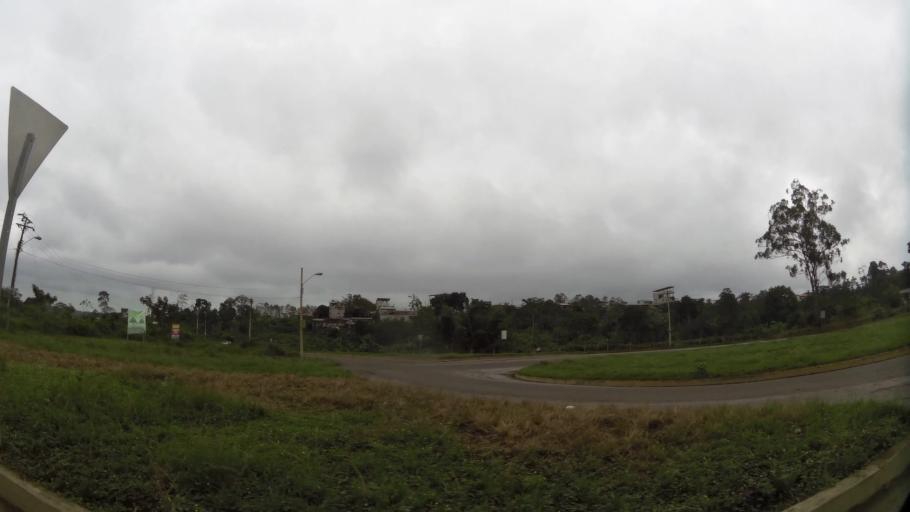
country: EC
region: El Oro
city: Pasaje
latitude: -3.3281
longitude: -79.7719
